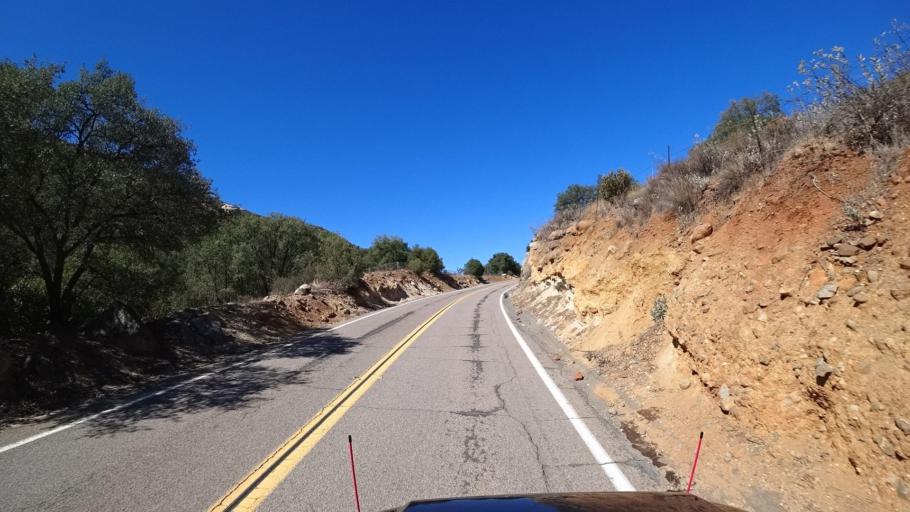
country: US
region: California
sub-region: San Diego County
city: Alpine
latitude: 32.7052
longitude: -116.7311
